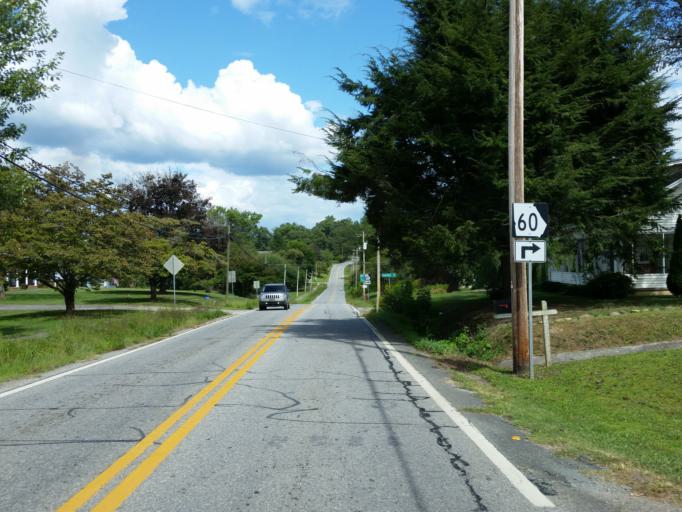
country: US
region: Georgia
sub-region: Fannin County
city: Blue Ridge
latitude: 34.8751
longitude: -84.2434
